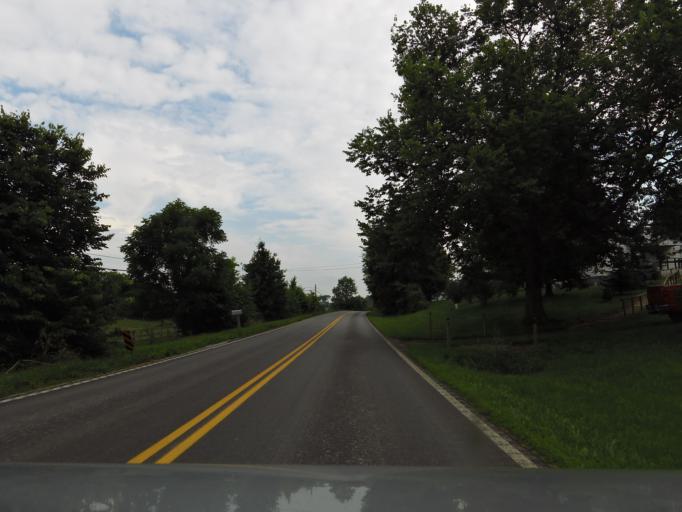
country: US
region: Kentucky
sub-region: Harrison County
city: Cynthiana
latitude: 38.4391
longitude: -84.2487
